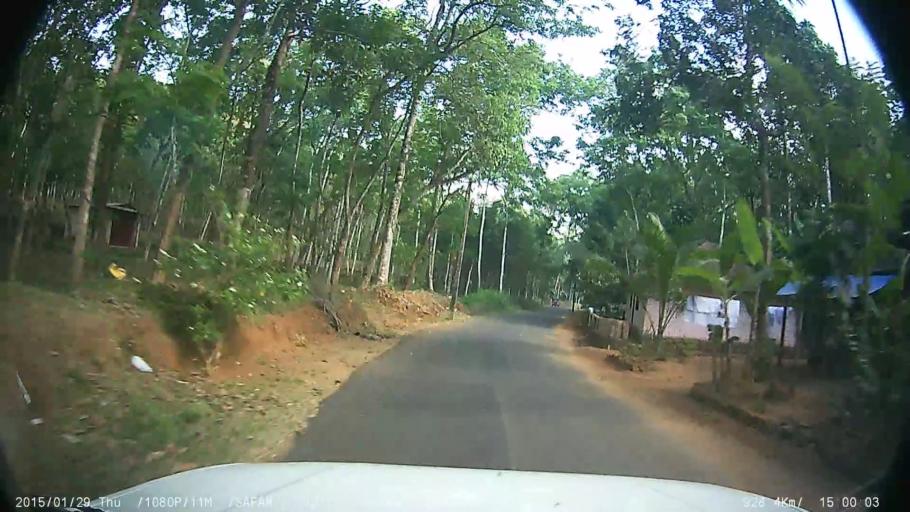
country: IN
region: Kerala
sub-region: Kottayam
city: Palackattumala
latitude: 9.7291
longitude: 76.5641
